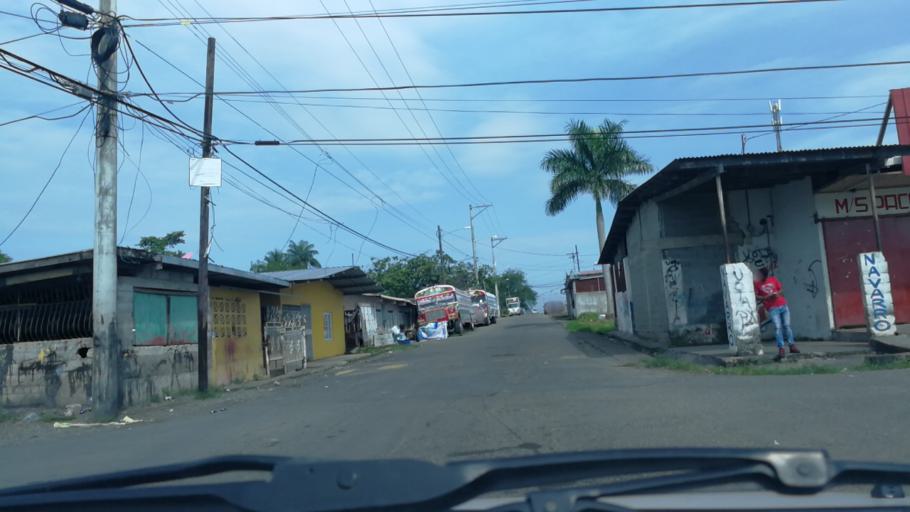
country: PA
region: Panama
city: Pacora
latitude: 9.0838
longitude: -79.2915
